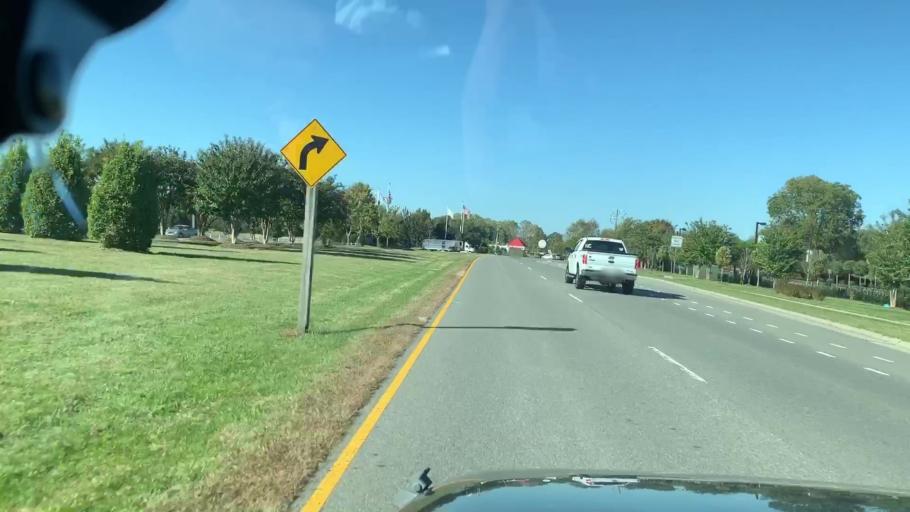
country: US
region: Virginia
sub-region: James City County
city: Williamsburg
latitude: 37.3511
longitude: -76.7629
